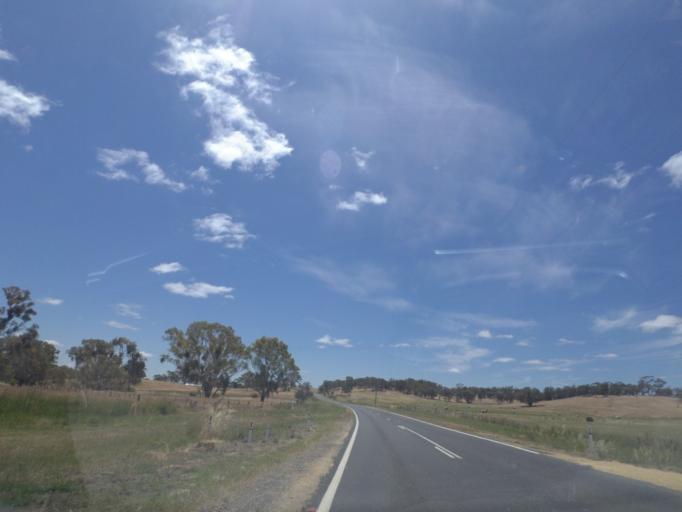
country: AU
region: Victoria
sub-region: Mount Alexander
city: Castlemaine
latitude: -37.2196
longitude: 144.1408
